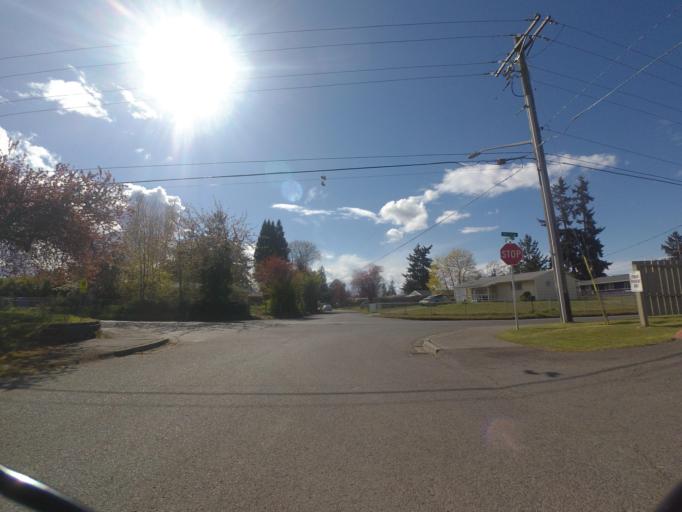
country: US
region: Washington
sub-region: Pierce County
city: Lakewood
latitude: 47.1636
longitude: -122.4993
